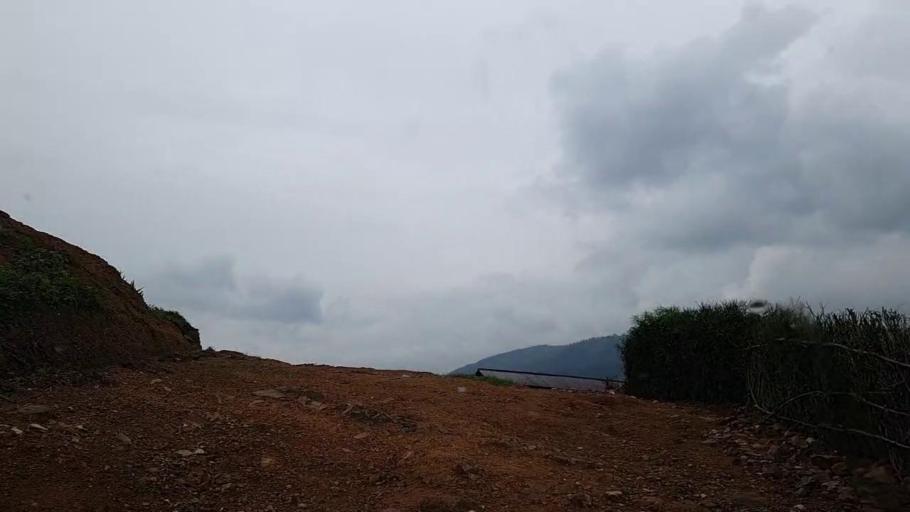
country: RW
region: Kigali
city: Kigali
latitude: -1.9020
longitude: 29.9552
